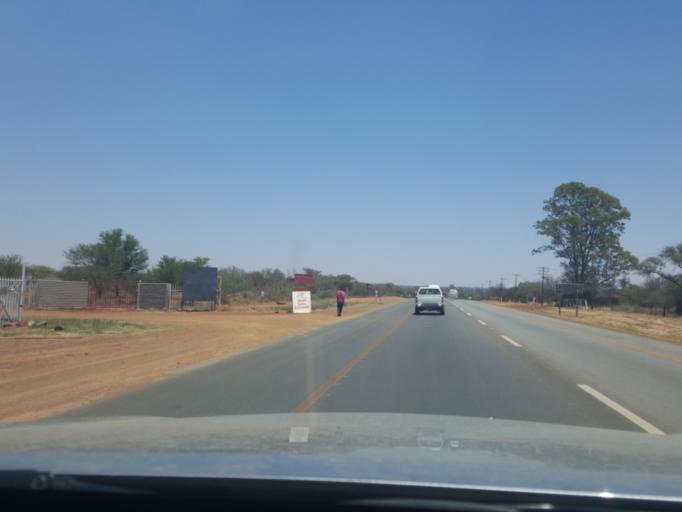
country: ZA
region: North-West
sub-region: Ngaka Modiri Molema District Municipality
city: Zeerust
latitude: -25.5557
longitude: 26.0682
